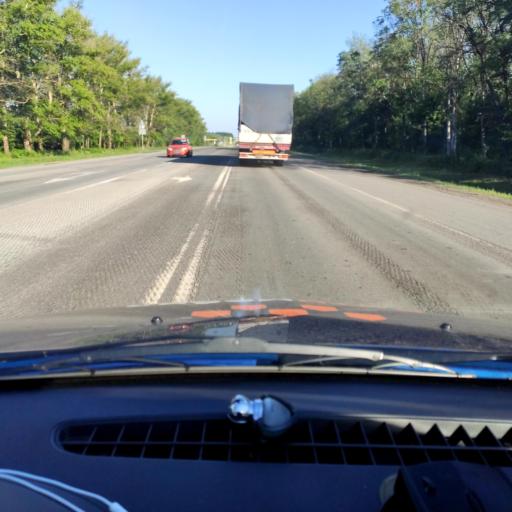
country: RU
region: Orjol
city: Zmiyevka
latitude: 52.7072
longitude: 36.3612
